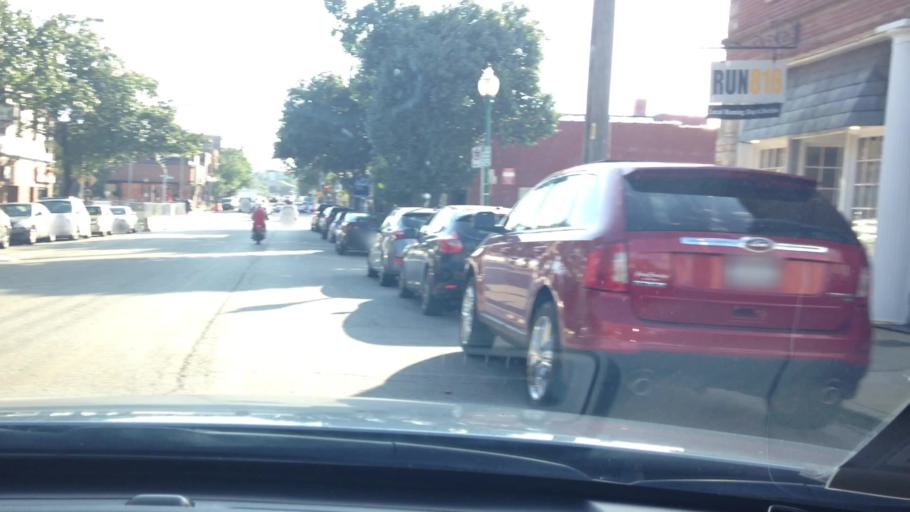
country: US
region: Kansas
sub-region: Johnson County
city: Westwood
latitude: 39.0539
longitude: -94.5893
